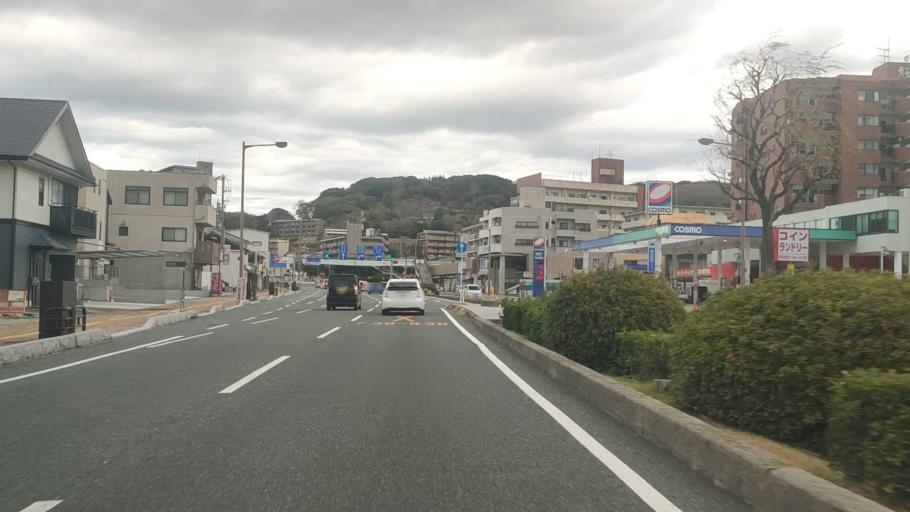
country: JP
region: Yamaguchi
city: Shimonoseki
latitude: 33.9664
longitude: 130.9416
